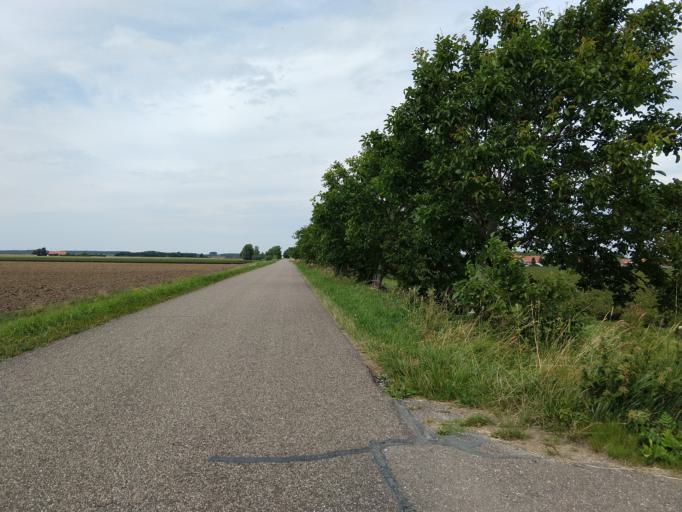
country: NL
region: Zeeland
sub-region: Gemeente Borsele
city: Borssele
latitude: 51.4889
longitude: 3.7427
